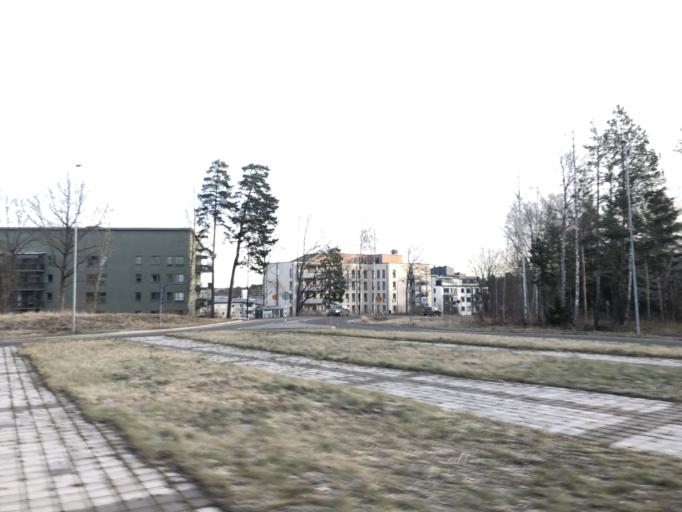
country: SE
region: Stockholm
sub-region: Jarfalla Kommun
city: Jakobsberg
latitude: 59.4090
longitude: 17.7967
